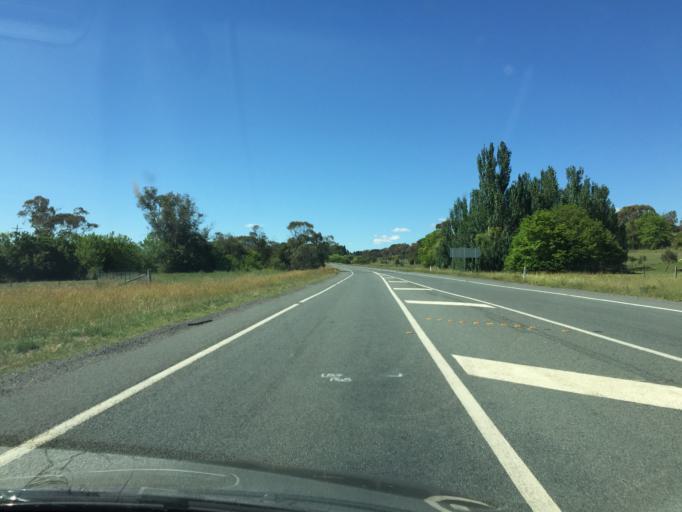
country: AU
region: Australian Capital Territory
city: Macarthur
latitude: -35.4992
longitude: 149.1501
